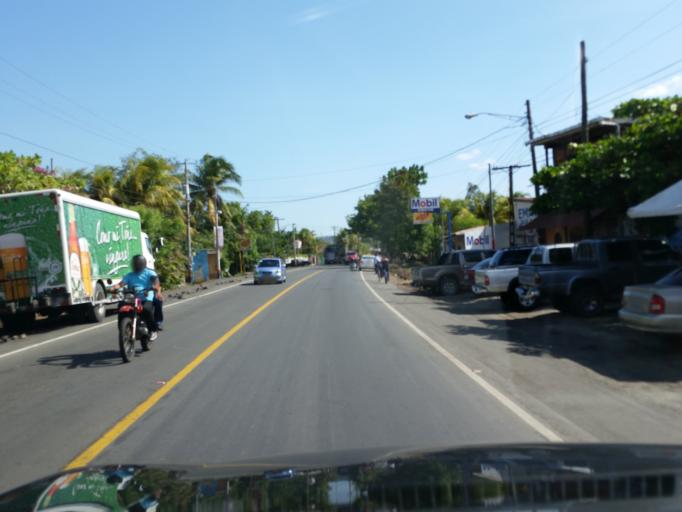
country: NI
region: Leon
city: Leon
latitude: 12.4258
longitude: -86.8660
